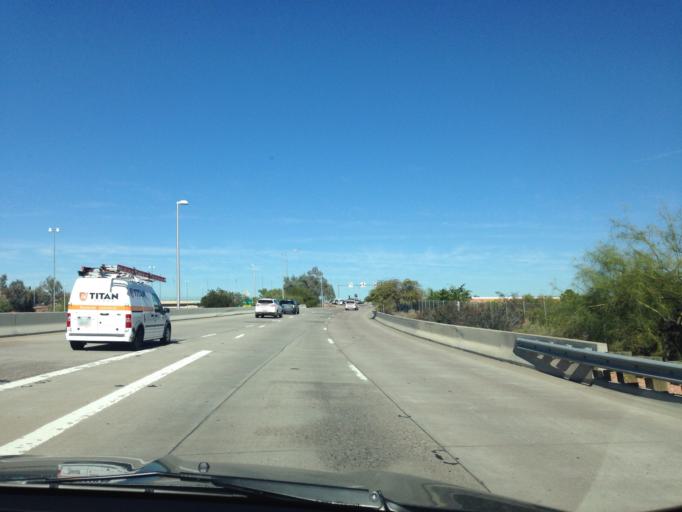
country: US
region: Arizona
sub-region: Maricopa County
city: Glendale
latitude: 33.6592
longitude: -112.1138
